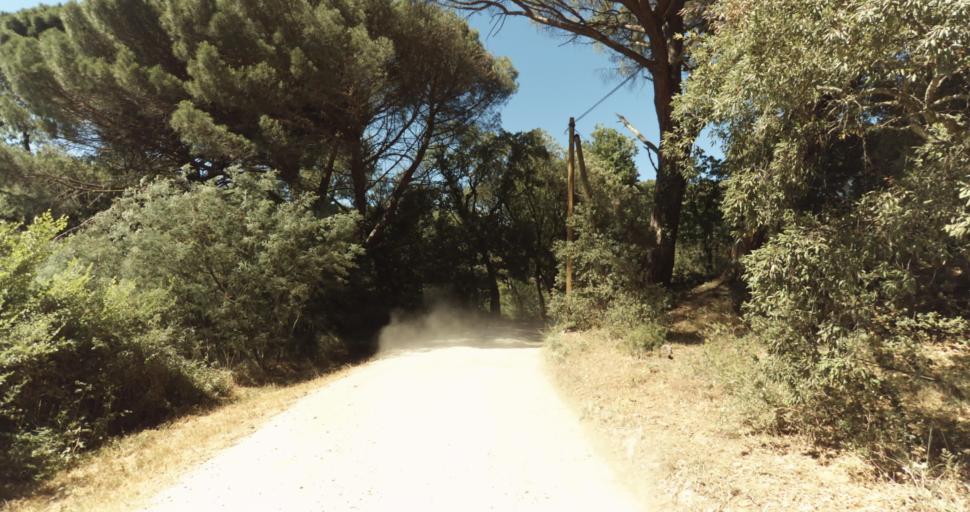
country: FR
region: Provence-Alpes-Cote d'Azur
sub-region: Departement du Var
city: La Croix-Valmer
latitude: 43.2297
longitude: 6.5595
